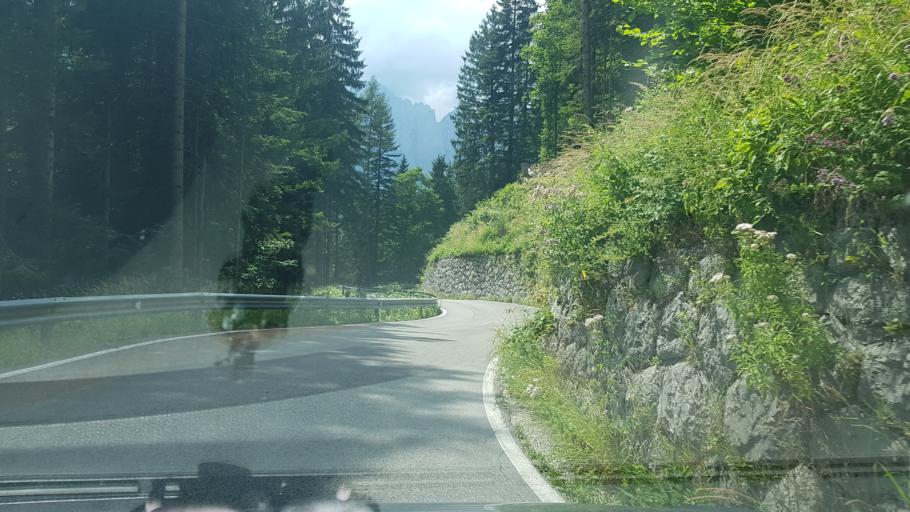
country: IT
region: Friuli Venezia Giulia
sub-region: Provincia di Udine
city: Pontebba
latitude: 46.4979
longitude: 13.2276
